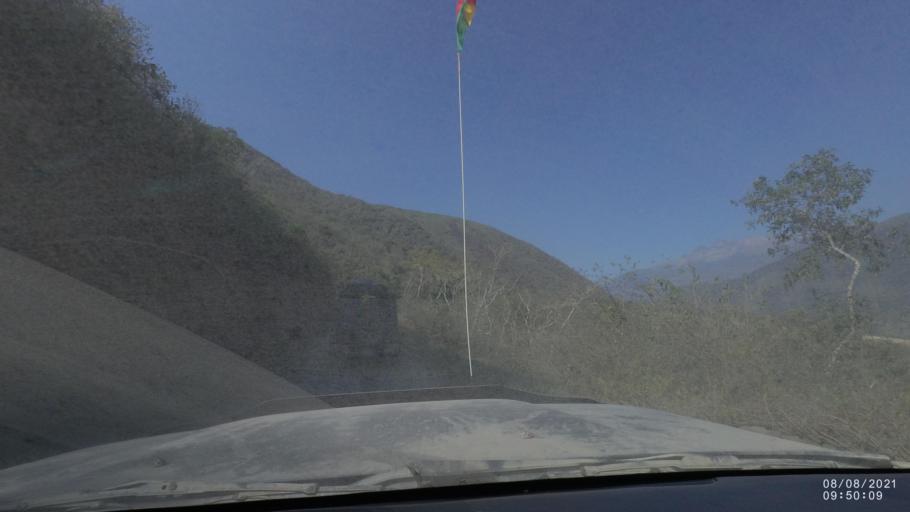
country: BO
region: La Paz
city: Quime
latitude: -16.6196
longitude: -66.7286
